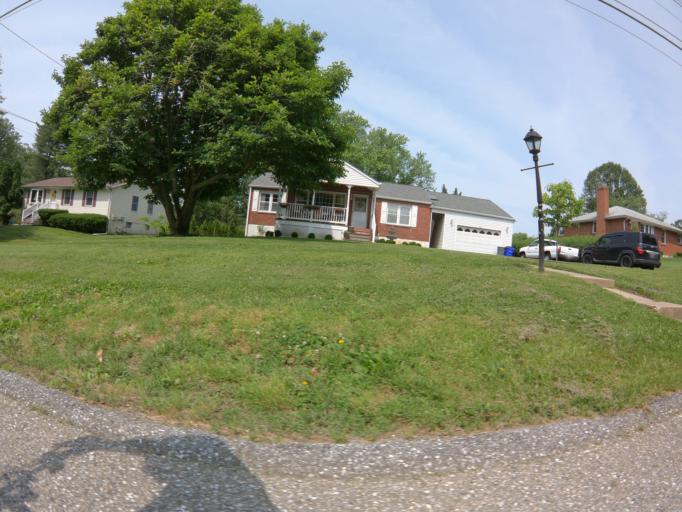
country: US
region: Maryland
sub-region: Howard County
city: Columbia
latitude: 39.2320
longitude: -76.8088
